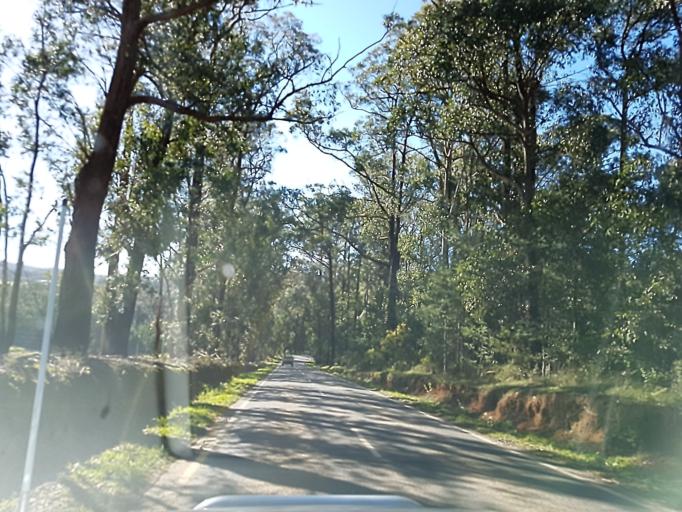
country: AU
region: Victoria
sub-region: Yarra Ranges
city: Healesville
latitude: -37.5340
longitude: 145.4595
